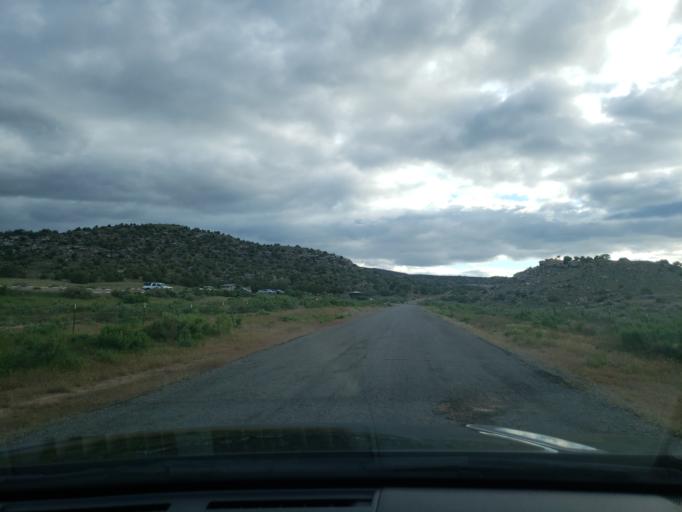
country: US
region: Colorado
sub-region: Mesa County
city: Fruita
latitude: 39.1409
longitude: -108.7549
